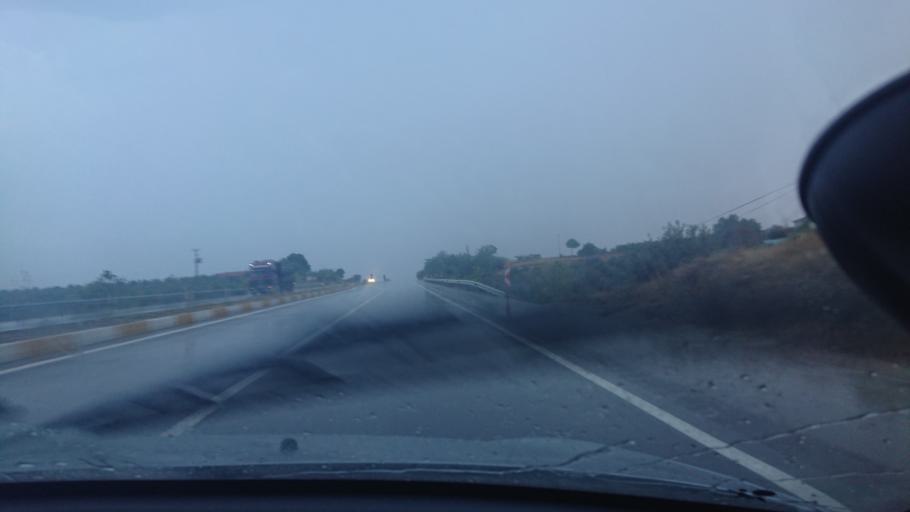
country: TR
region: Manisa
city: Menye
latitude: 38.5318
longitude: 28.4054
